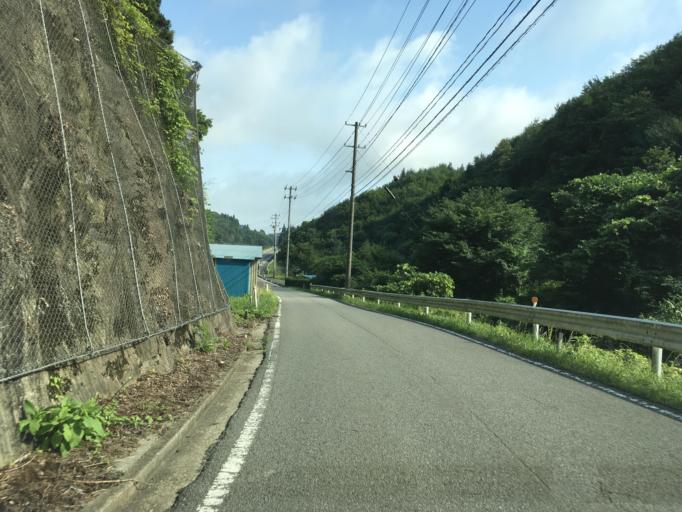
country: JP
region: Iwate
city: Ofunato
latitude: 38.9080
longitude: 141.6212
